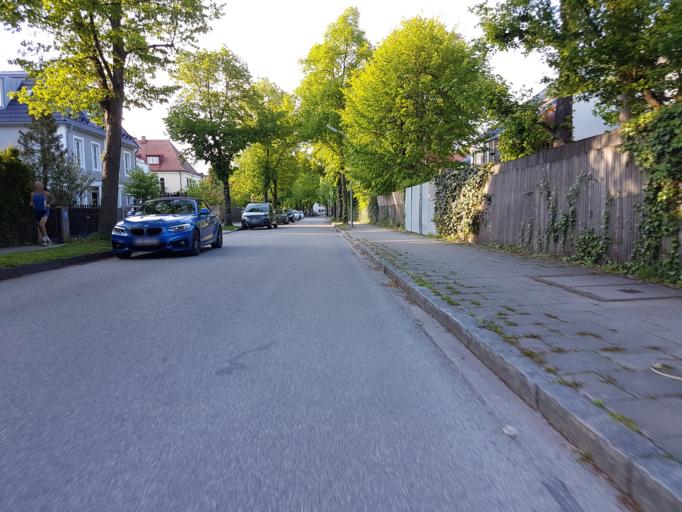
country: DE
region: Bavaria
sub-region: Upper Bavaria
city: Pasing
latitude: 48.1582
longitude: 11.4627
